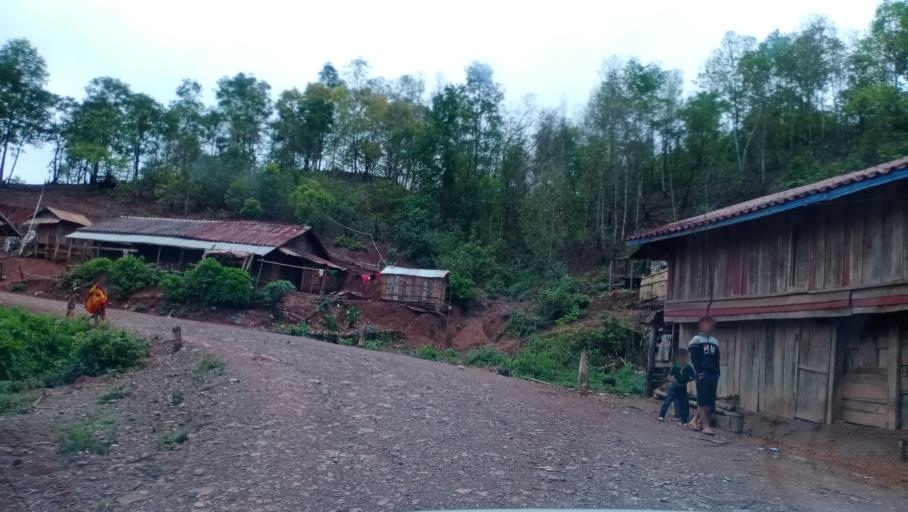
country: LA
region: Phongsali
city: Phongsali
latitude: 21.3381
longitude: 102.0826
